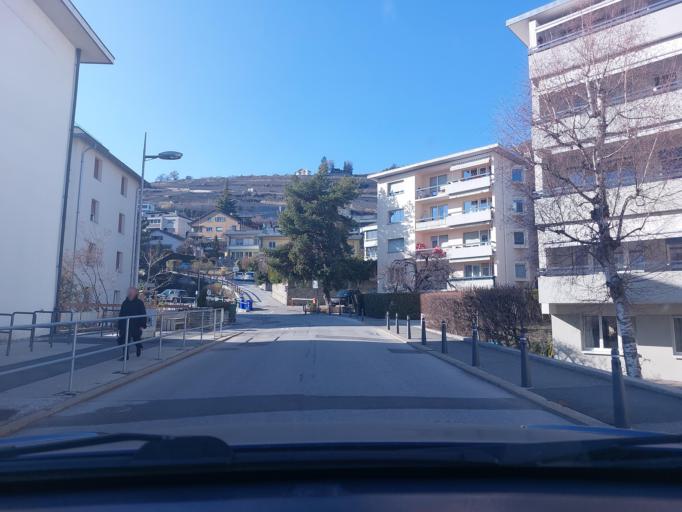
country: CH
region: Valais
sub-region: Sion District
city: Sitten
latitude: 46.2366
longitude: 7.3569
